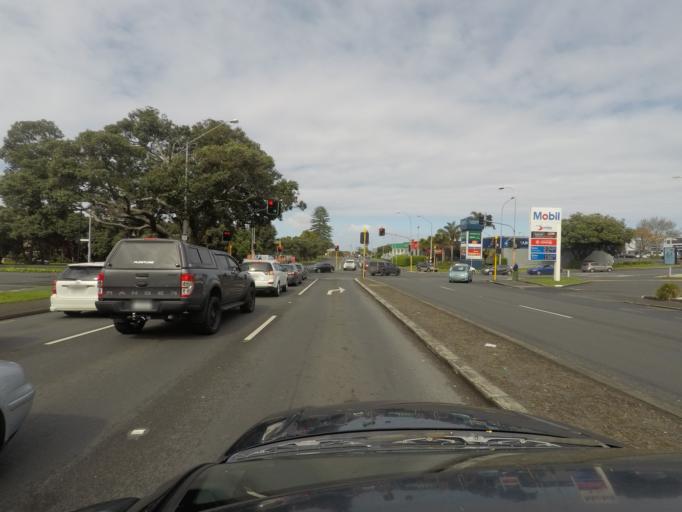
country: NZ
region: Auckland
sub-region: Auckland
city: Tamaki
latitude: -36.9081
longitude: 174.8390
